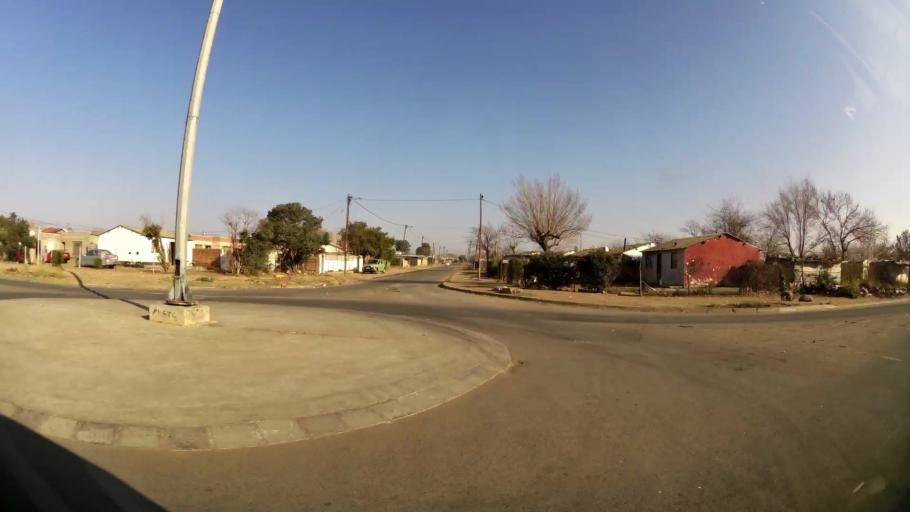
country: ZA
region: Orange Free State
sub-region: Mangaung Metropolitan Municipality
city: Bloemfontein
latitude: -29.1403
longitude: 26.2511
